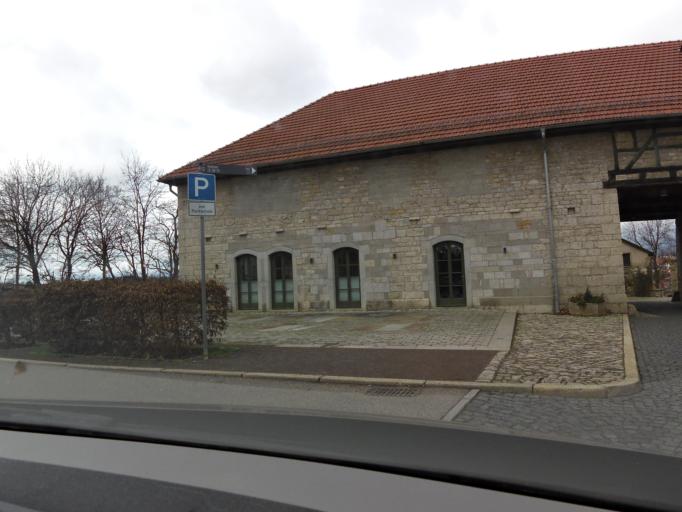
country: DE
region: Thuringia
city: Apolda
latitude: 51.0213
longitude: 11.5139
